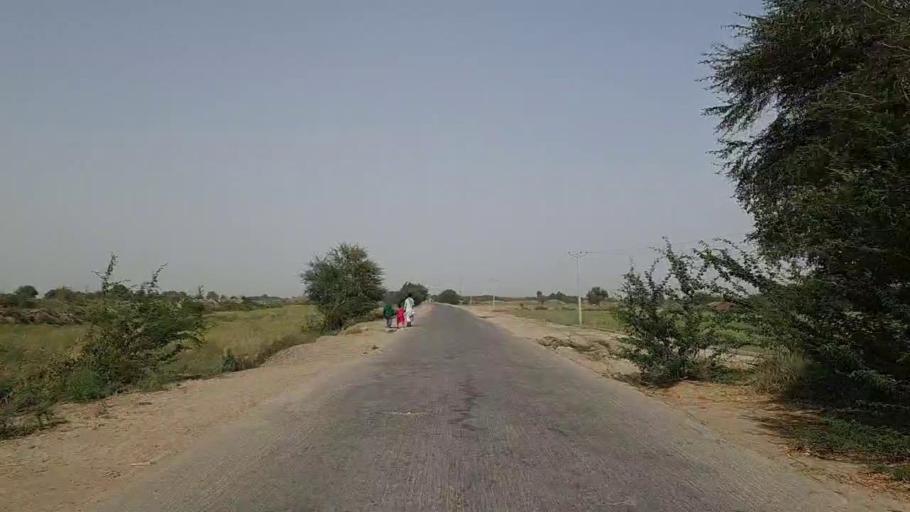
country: PK
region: Sindh
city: Tando Bago
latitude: 24.9152
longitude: 69.0980
